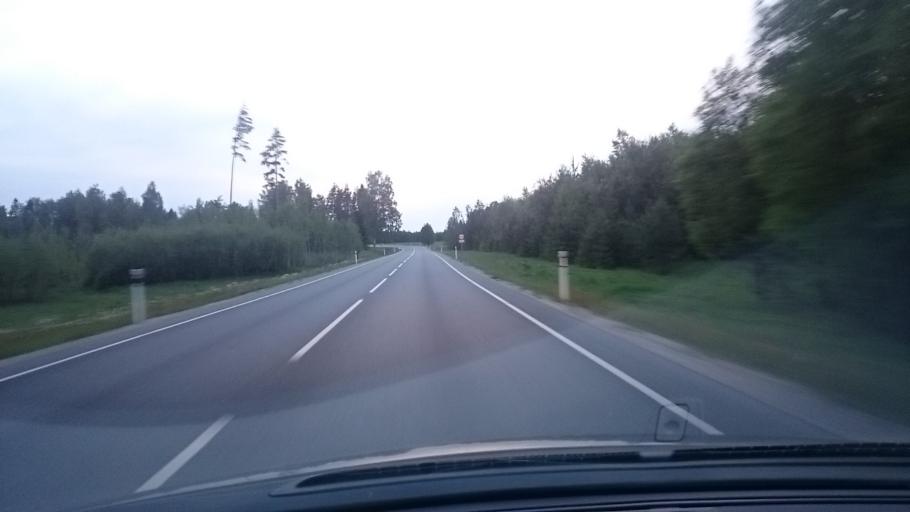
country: EE
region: Raplamaa
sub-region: Kehtna vald
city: Kehtna
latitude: 58.8981
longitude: 24.9021
